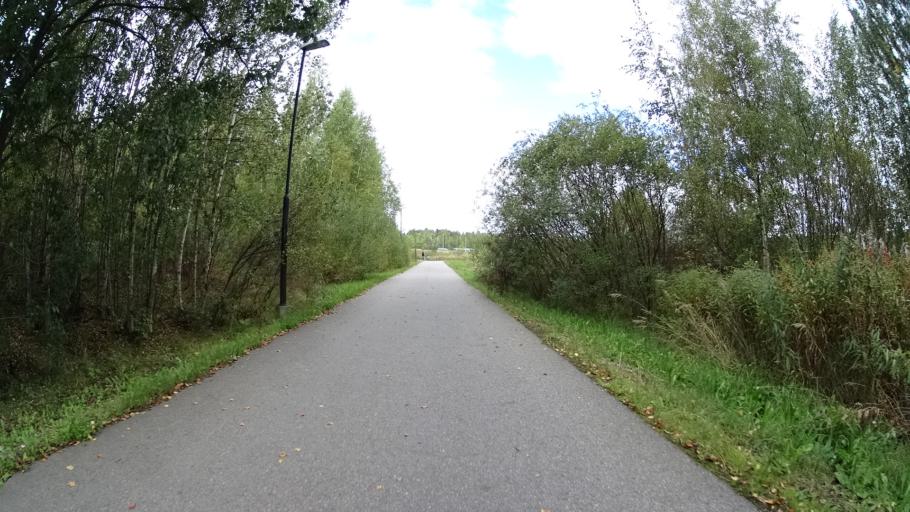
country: FI
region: Uusimaa
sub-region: Helsinki
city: Vantaa
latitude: 60.2440
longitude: 25.0202
